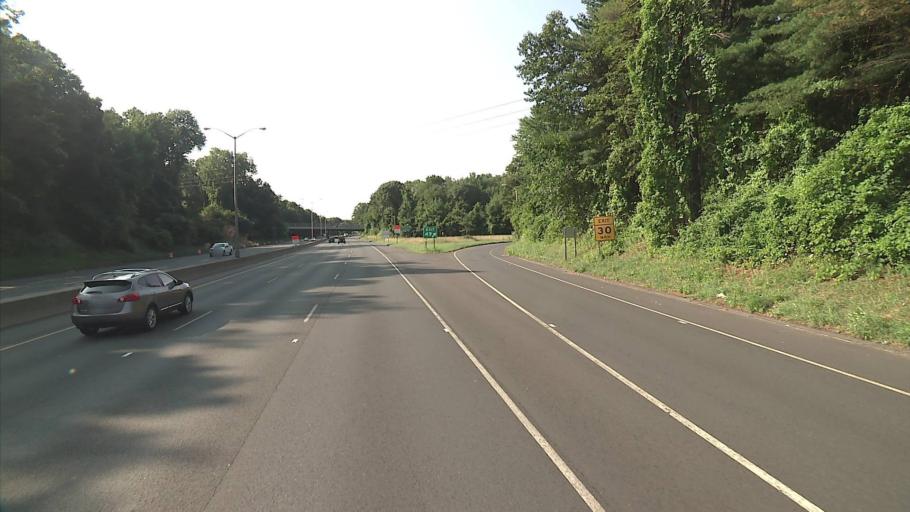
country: US
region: Connecticut
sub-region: Hartford County
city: Sherwood Manor
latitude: 42.0236
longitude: -72.5895
